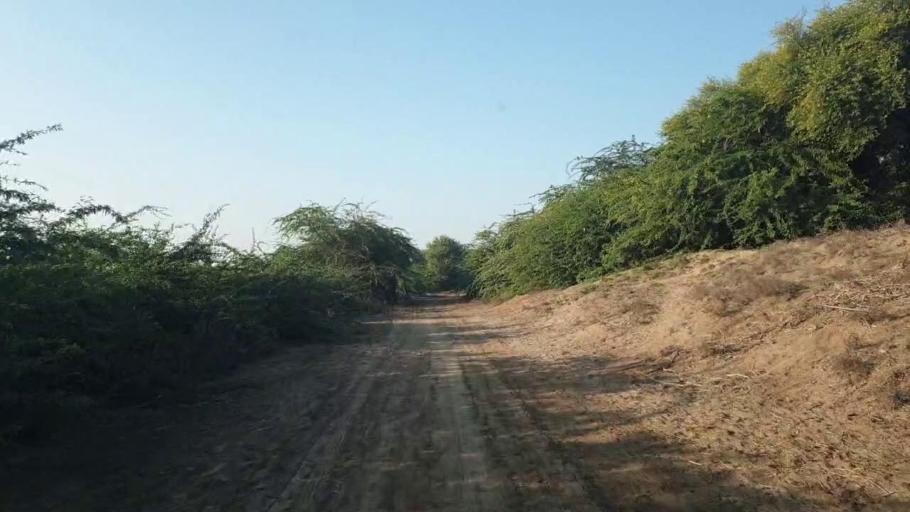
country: PK
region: Sindh
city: Badin
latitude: 24.6049
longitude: 68.7798
